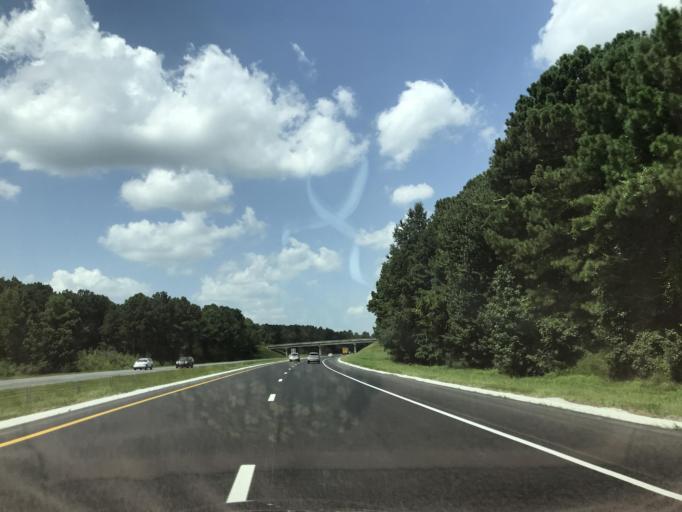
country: US
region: North Carolina
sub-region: Duplin County
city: Warsaw
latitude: 34.9571
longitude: -78.1004
